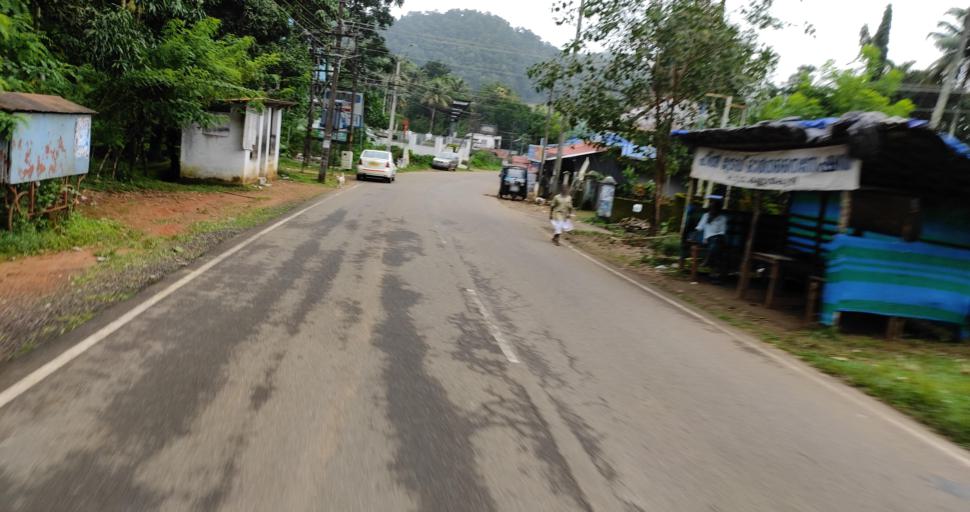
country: IN
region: Kerala
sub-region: Ernakulam
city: Angamali
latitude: 10.2886
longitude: 76.5583
